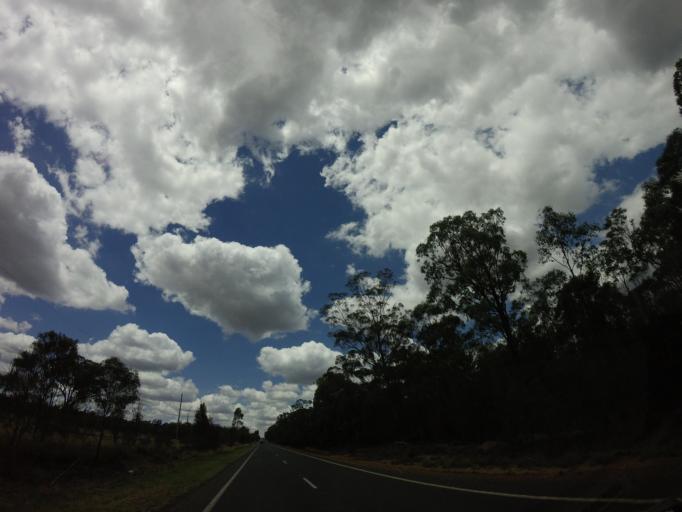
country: AU
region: Queensland
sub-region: Goondiwindi
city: Goondiwindi
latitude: -28.0040
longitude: 150.9315
